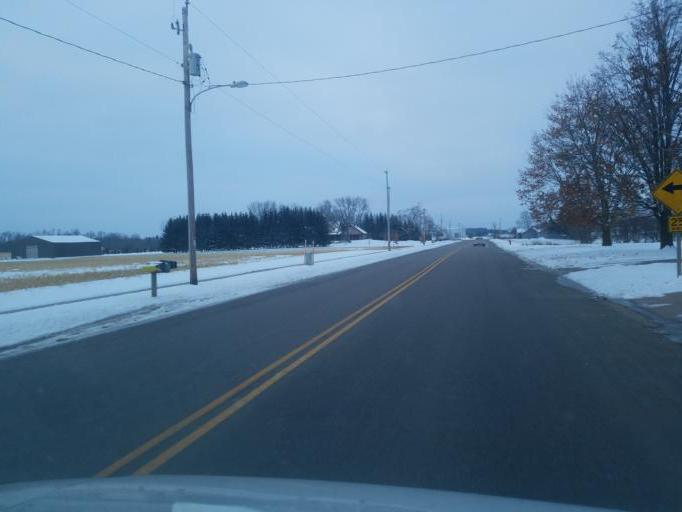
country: US
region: Wisconsin
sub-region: Waupaca County
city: Manawa
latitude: 44.4567
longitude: -88.9200
